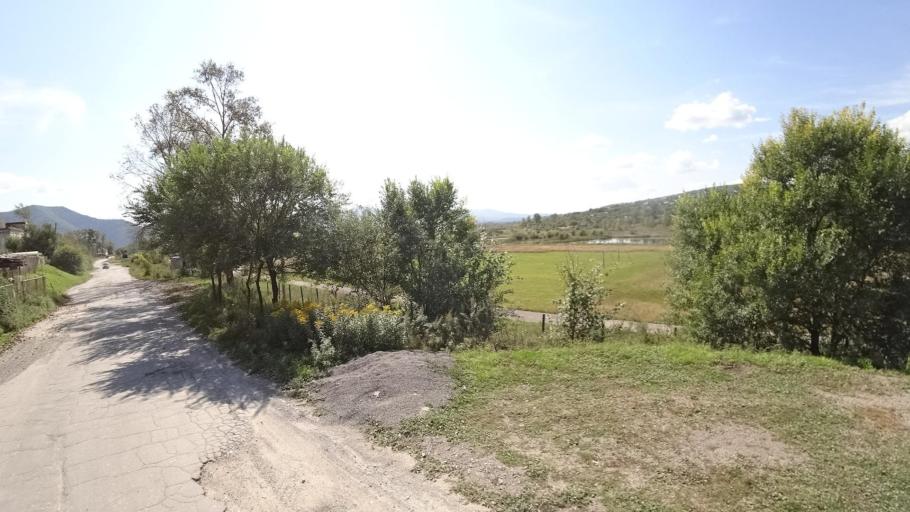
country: RU
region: Jewish Autonomous Oblast
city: Londoko
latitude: 49.0072
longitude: 131.8793
